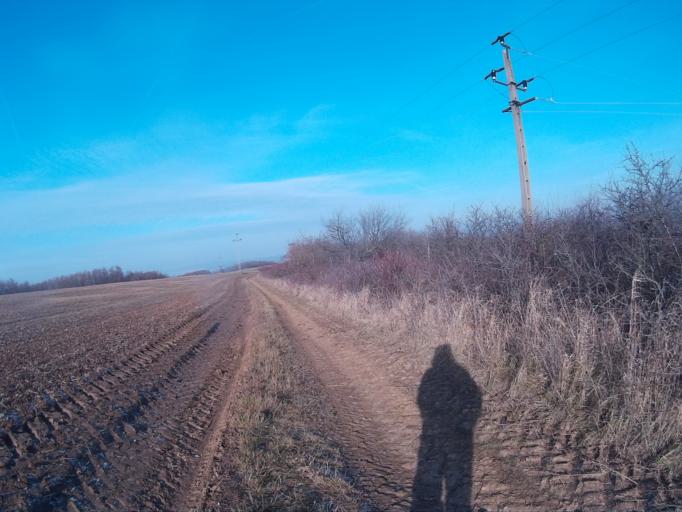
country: HU
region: Nograd
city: Bercel
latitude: 47.9351
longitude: 19.4287
